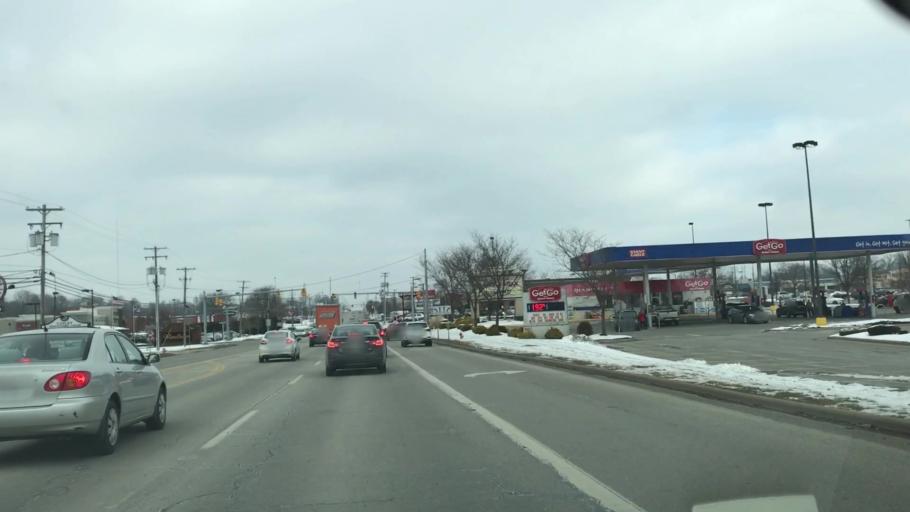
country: US
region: Ohio
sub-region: Mahoning County
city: Poland
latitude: 41.0272
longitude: -80.6344
